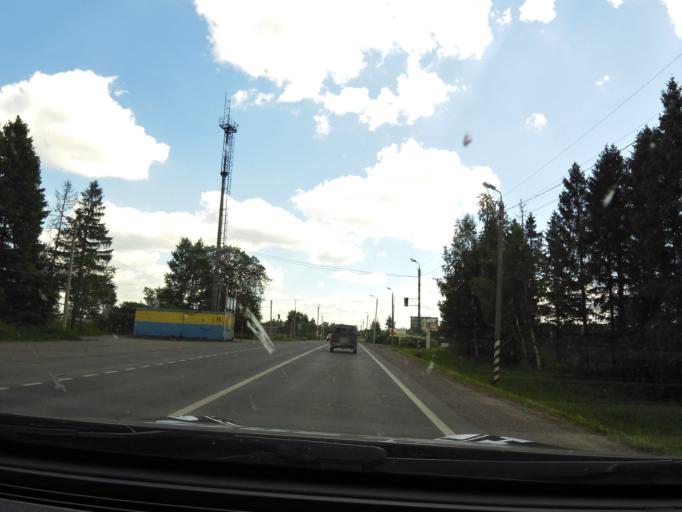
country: RU
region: Vologda
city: Vologda
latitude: 59.2431
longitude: 39.7850
